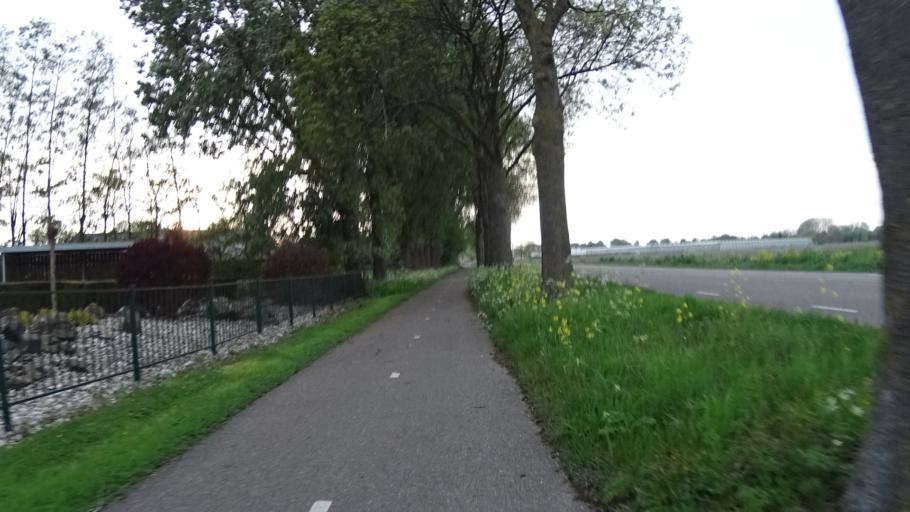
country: NL
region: North Brabant
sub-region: Gemeente Woudrichem
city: Woudrichem
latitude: 51.7829
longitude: 5.0383
